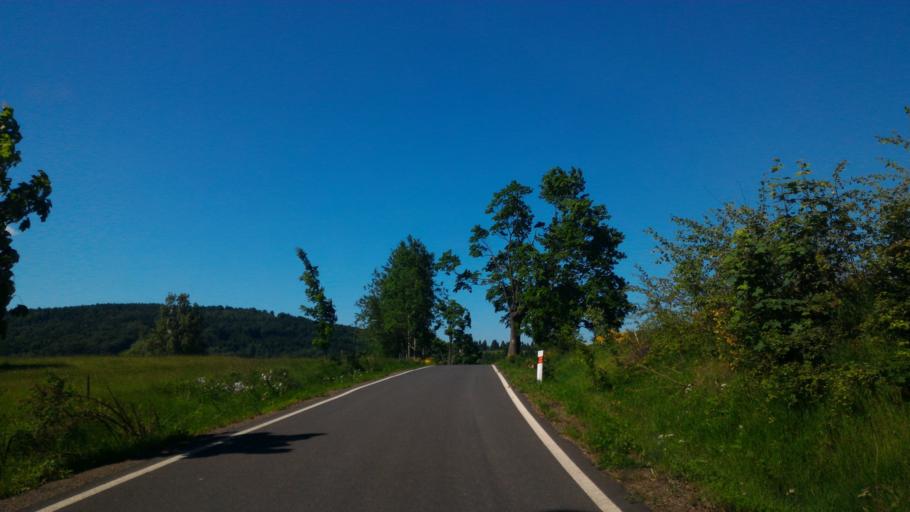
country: DE
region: Saxony
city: Kurort Jonsdorf
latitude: 50.8218
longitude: 14.7009
